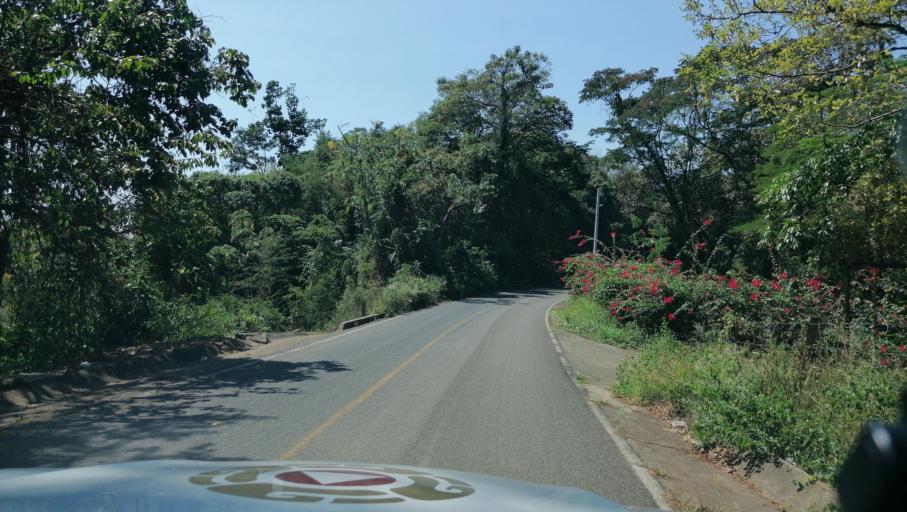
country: MX
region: Chiapas
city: Veinte de Noviembre
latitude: 15.0041
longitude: -92.2298
